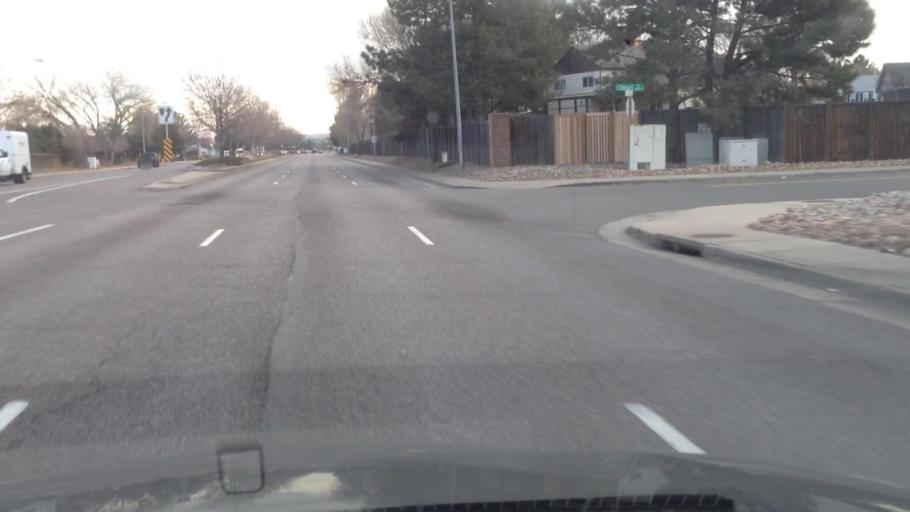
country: US
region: Colorado
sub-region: Adams County
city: Aurora
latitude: 39.6746
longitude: -104.8156
